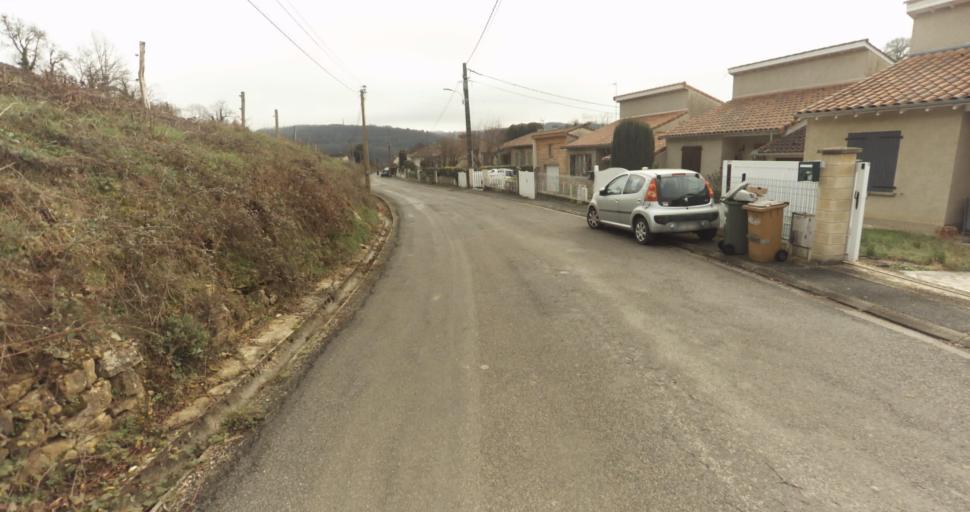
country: FR
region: Midi-Pyrenees
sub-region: Departement du Lot
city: Figeac
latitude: 44.6150
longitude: 2.0161
